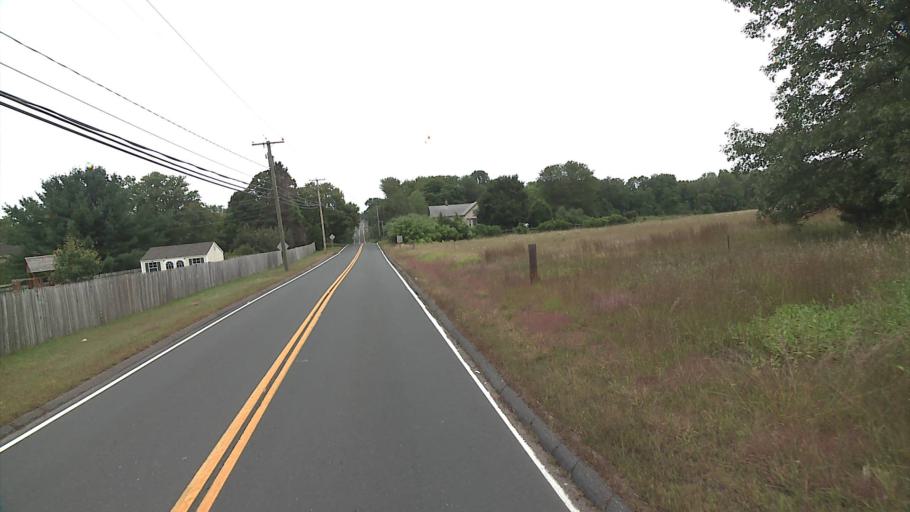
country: US
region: Connecticut
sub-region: Tolland County
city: Rockville
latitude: 41.8256
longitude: -72.4633
